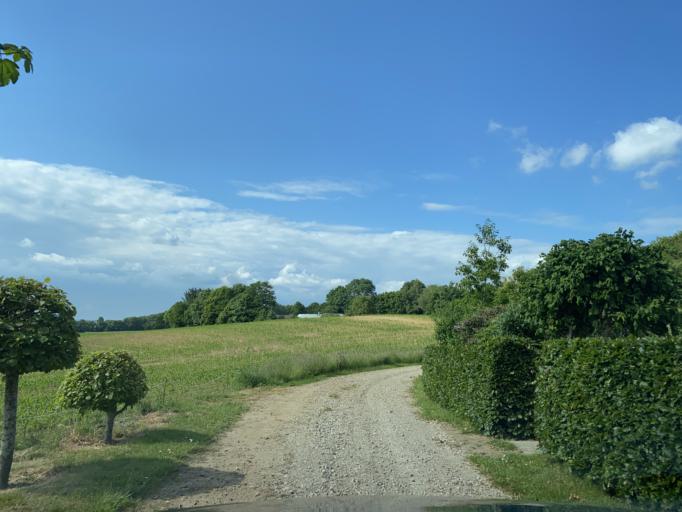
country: DK
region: Central Jutland
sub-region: Silkeborg Kommune
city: Svejbaek
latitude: 56.2396
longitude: 9.6905
